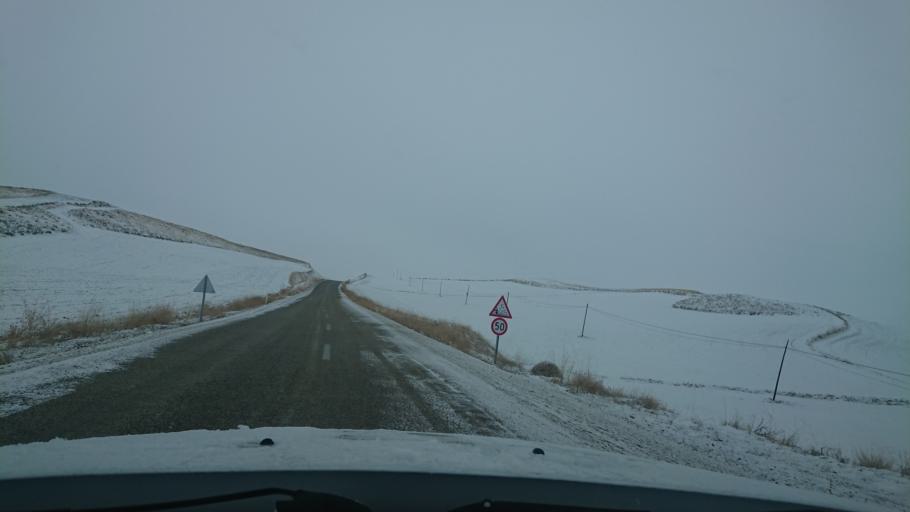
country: TR
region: Aksaray
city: Agacoren
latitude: 38.7882
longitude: 33.8712
